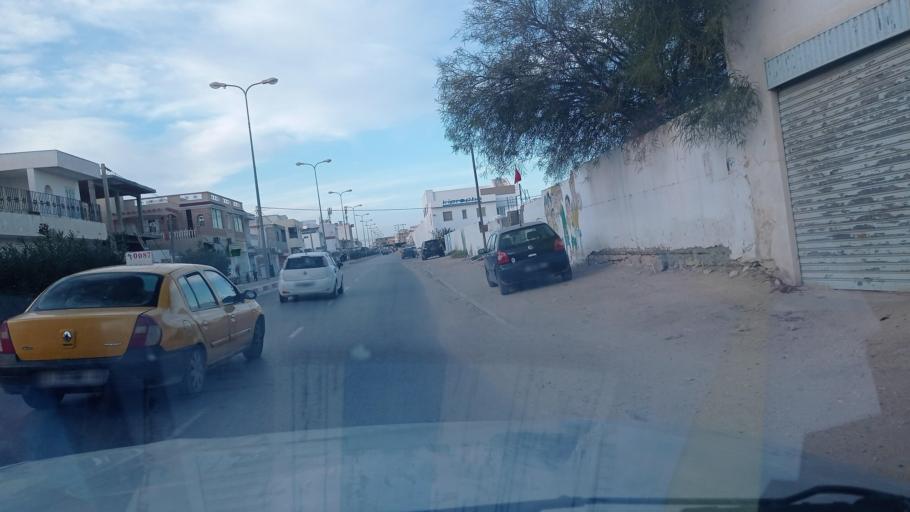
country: TN
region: Qabis
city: Gabes
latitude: 33.8419
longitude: 10.1140
